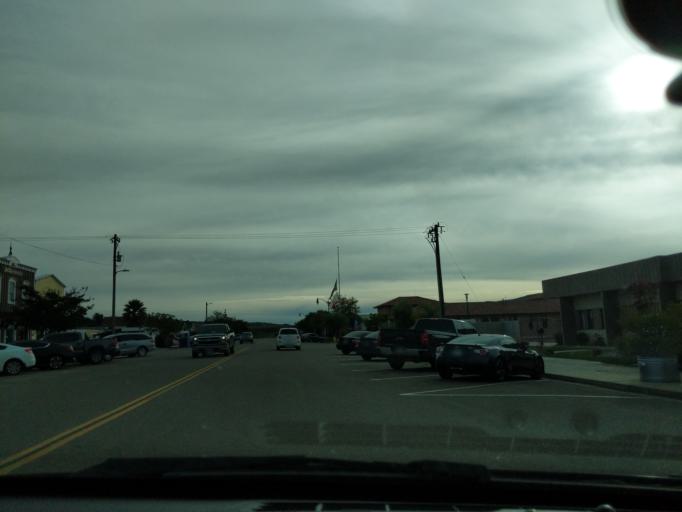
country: US
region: California
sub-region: Santa Barbara County
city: Orcutt
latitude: 34.8648
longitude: -120.4472
